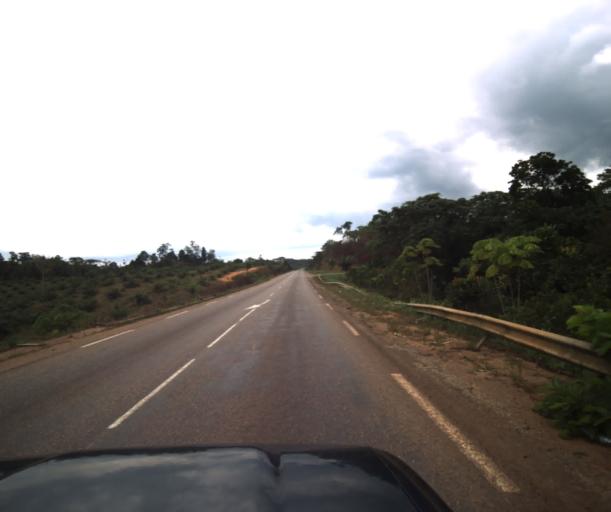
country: CM
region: Littoral
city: Edea
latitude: 3.8665
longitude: 10.0745
